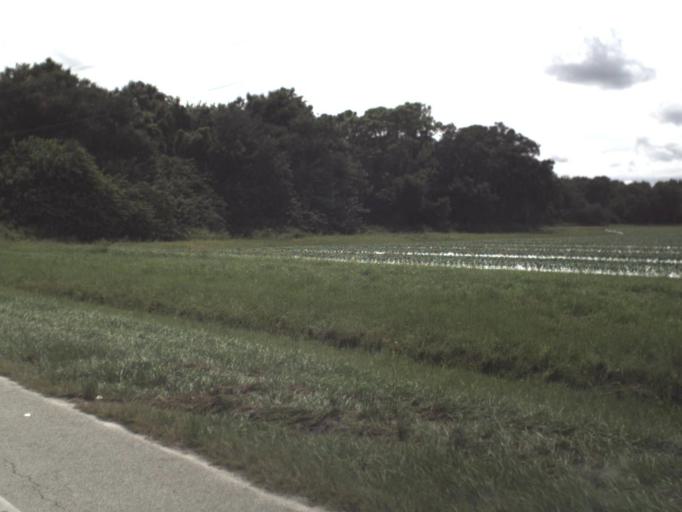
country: US
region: Florida
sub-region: Manatee County
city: Ellenton
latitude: 27.5928
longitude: -82.4255
